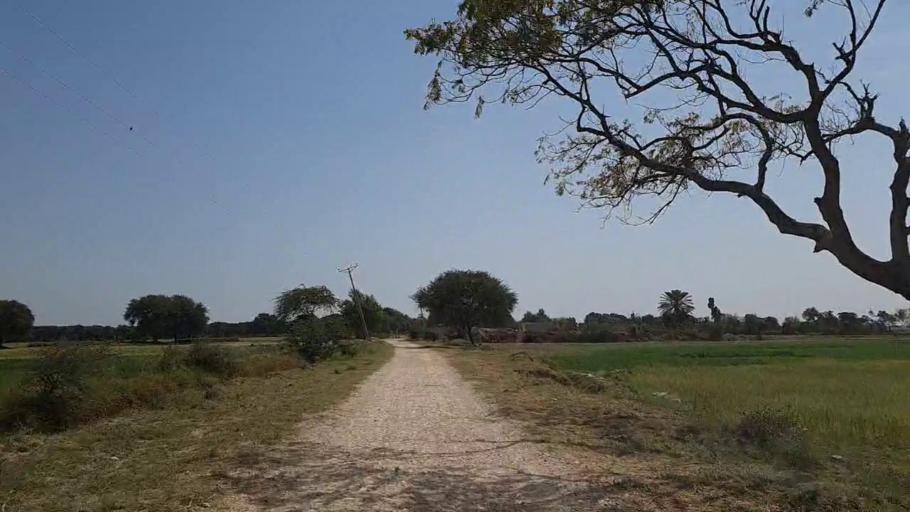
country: PK
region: Sindh
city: Mirpur Batoro
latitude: 24.7744
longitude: 68.2459
